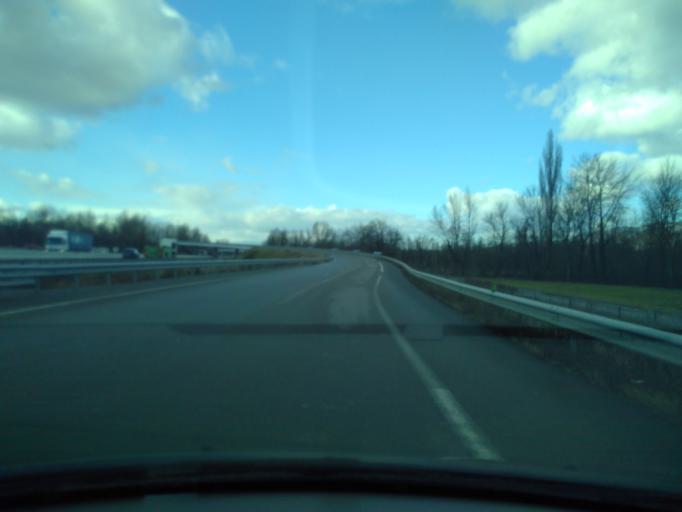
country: FR
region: Rhone-Alpes
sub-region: Departement de la Haute-Savoie
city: Contamine-sur-Arve
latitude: 46.1181
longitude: 6.3335
